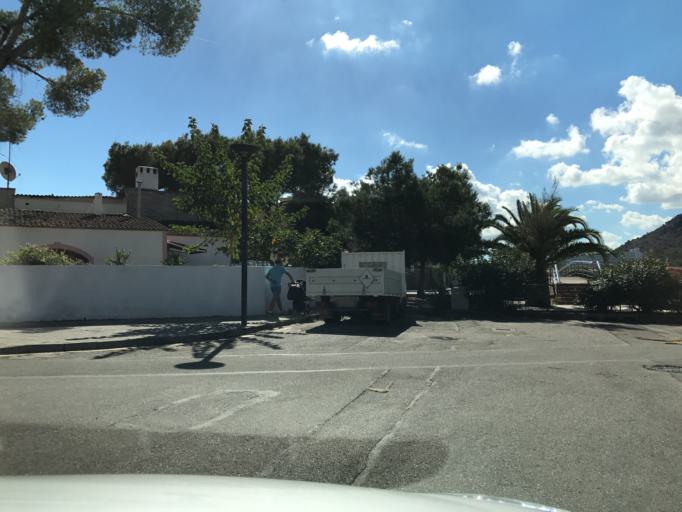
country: ES
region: Balearic Islands
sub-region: Illes Balears
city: Alcudia
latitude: 39.8365
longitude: 3.1102
